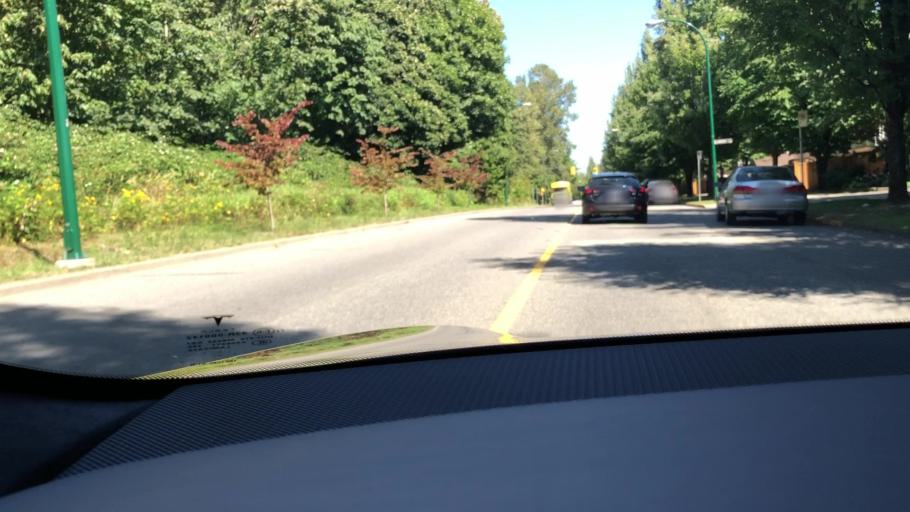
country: CA
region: British Columbia
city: Vancouver
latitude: 49.2085
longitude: -123.0331
